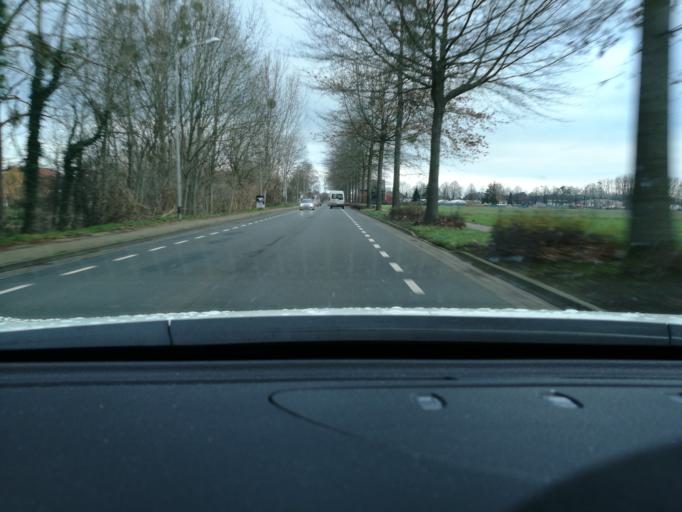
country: DE
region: Lower Saxony
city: Stadthagen
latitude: 52.3240
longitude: 9.2155
